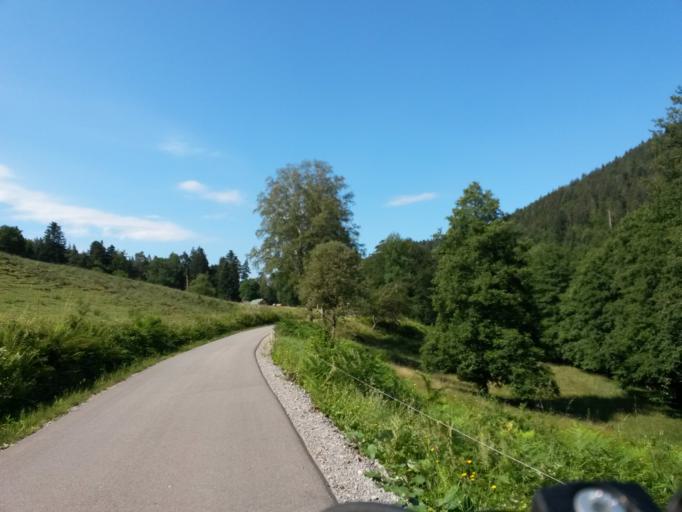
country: DE
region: Baden-Wuerttemberg
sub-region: Karlsruhe Region
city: Enzklosterle
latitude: 48.6779
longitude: 8.4825
